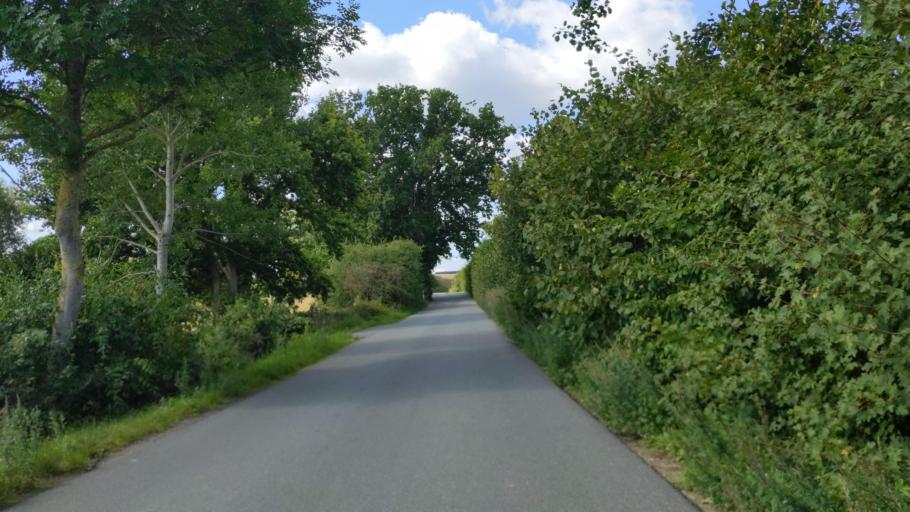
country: DE
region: Schleswig-Holstein
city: Kasseedorf
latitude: 54.1191
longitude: 10.7169
